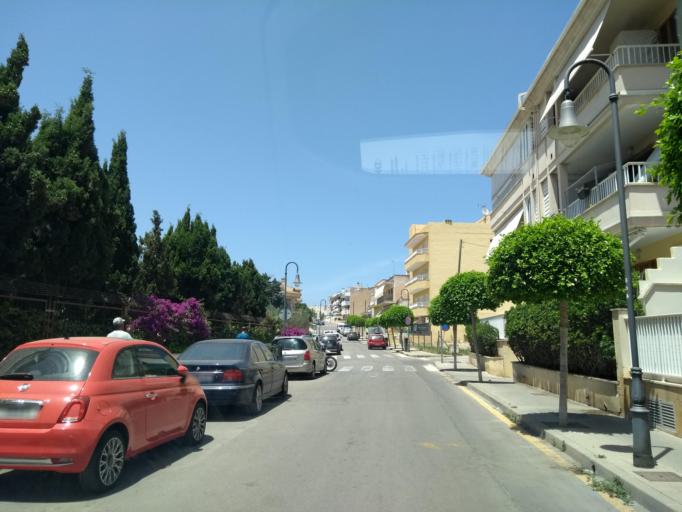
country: ES
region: Balearic Islands
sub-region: Illes Balears
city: Port d'Alcudia
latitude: 39.8411
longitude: 3.1383
